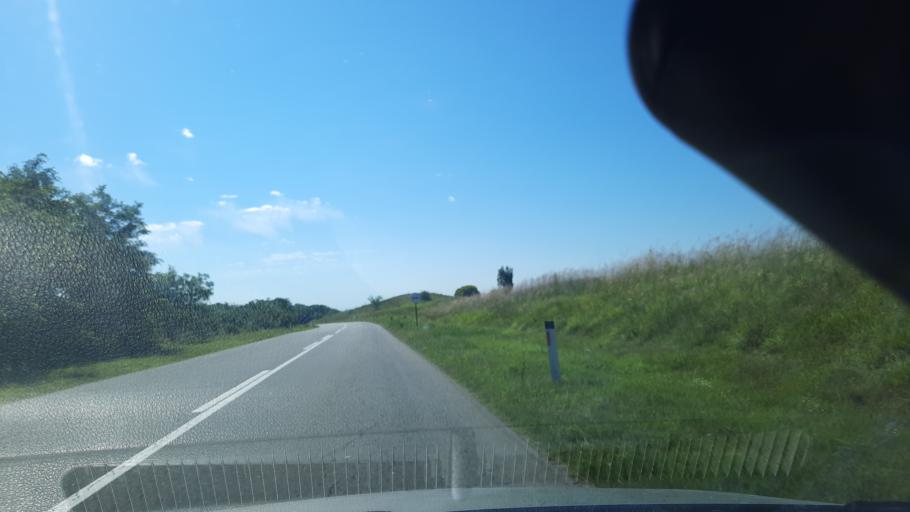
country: RS
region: Central Serbia
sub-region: Branicevski Okrug
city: Pozarevac
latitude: 44.8093
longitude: 21.1650
